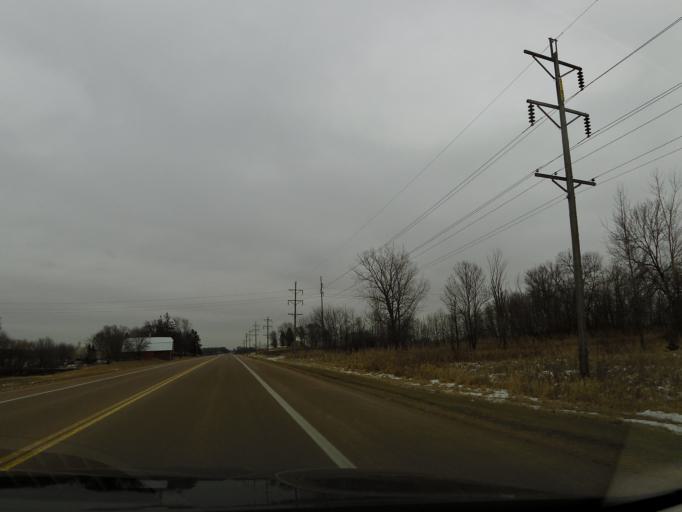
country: US
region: Minnesota
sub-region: Carver County
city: Watertown
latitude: 44.9631
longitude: -93.8206
